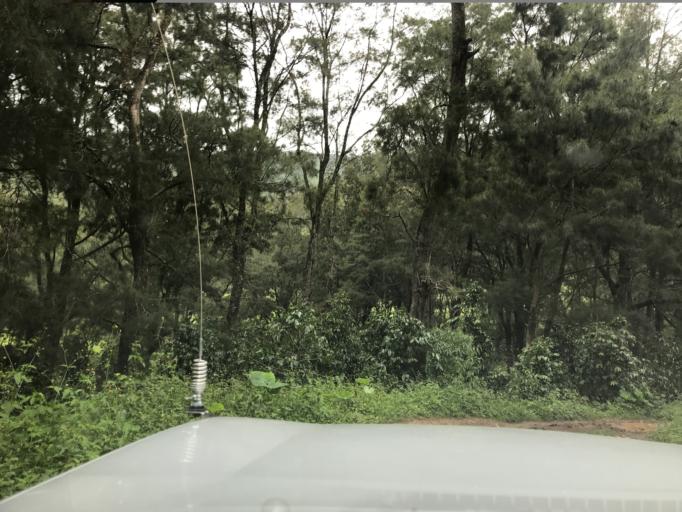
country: TL
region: Aileu
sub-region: Aileu Villa
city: Aileu
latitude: -8.8621
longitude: 125.5651
